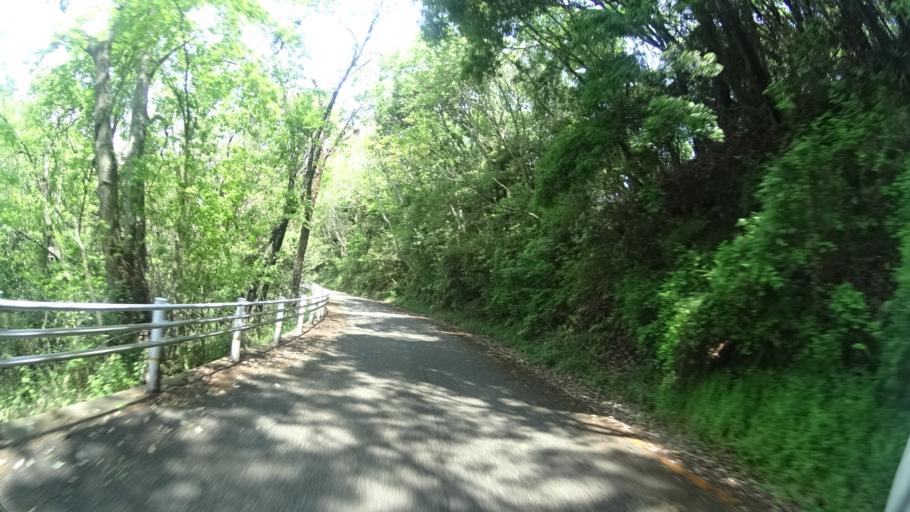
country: JP
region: Tokushima
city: Tokushima-shi
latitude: 34.0659
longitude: 134.5276
